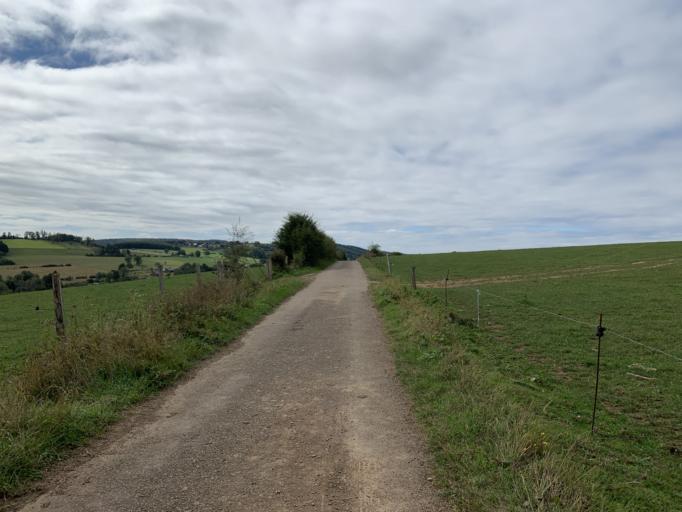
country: BE
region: Wallonia
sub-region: Province du Luxembourg
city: Tellin
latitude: 50.0986
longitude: 5.2803
